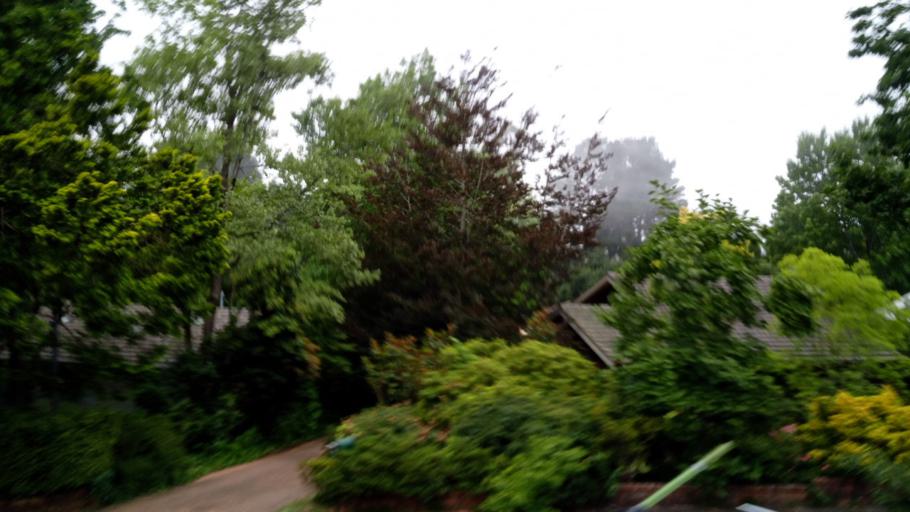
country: AU
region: New South Wales
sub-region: Blue Mountains Municipality
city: Leura
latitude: -33.7203
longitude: 150.3291
